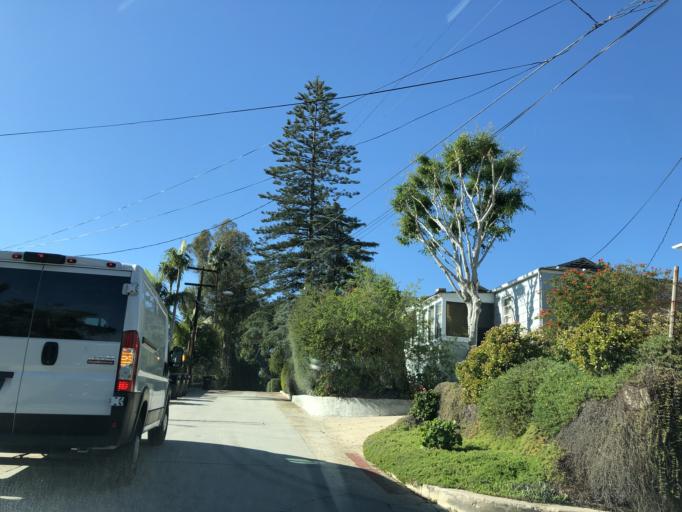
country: US
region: California
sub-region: San Diego County
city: San Diego
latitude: 32.7339
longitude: -117.1309
